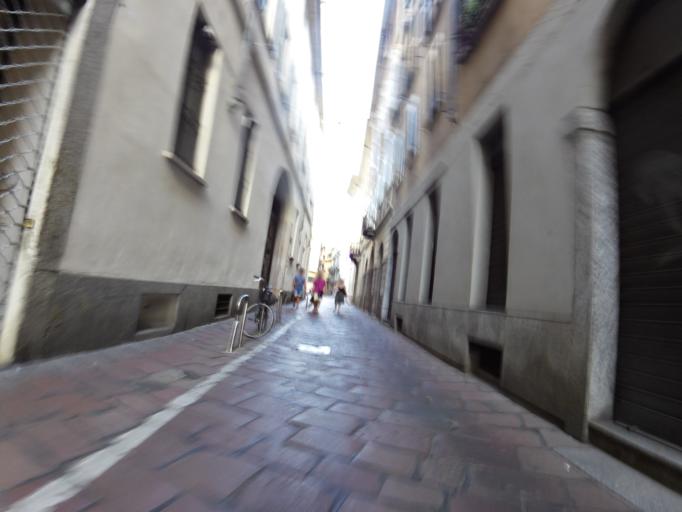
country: IT
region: Lombardy
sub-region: Citta metropolitana di Milano
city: Milano
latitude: 45.4624
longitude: 9.1837
